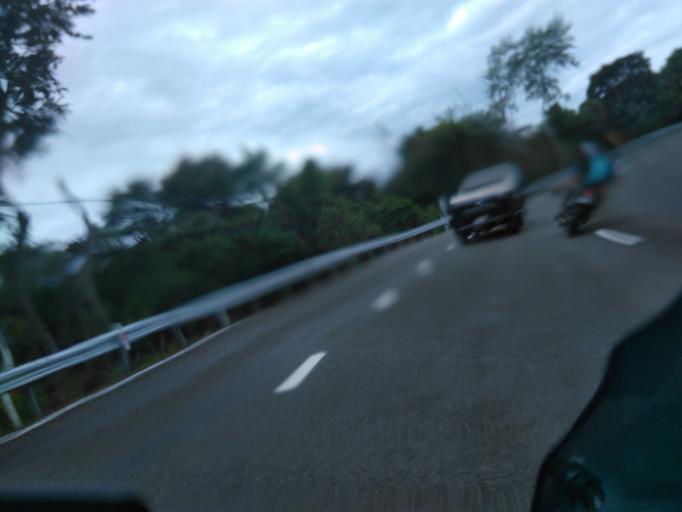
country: NZ
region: Gisborne
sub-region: Gisborne District
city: Gisborne
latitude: -38.4735
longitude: 177.6753
